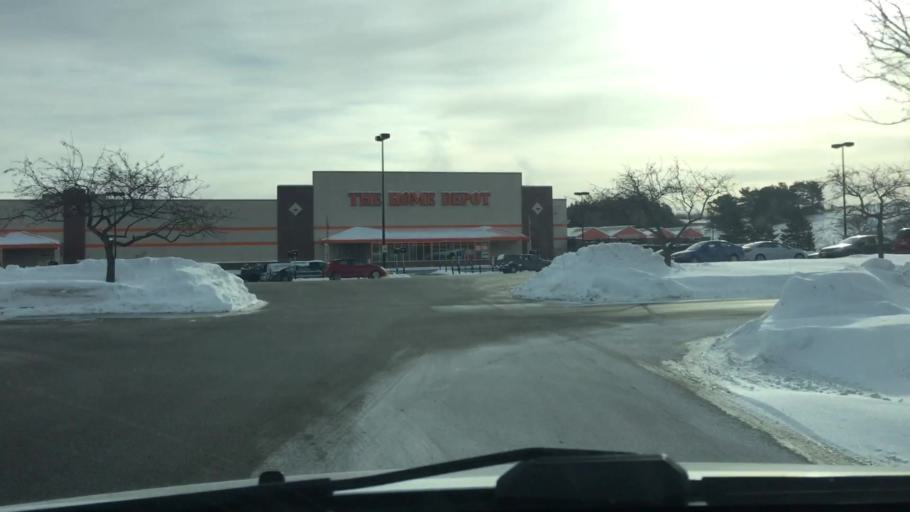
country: US
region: Wisconsin
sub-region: Waukesha County
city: Delafield
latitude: 43.0492
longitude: -88.3639
